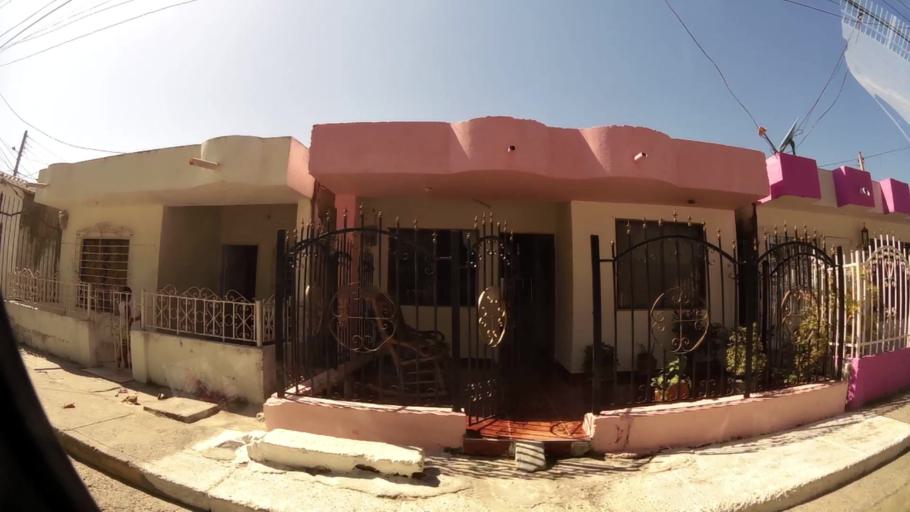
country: CO
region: Bolivar
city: Cartagena
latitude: 10.4381
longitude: -75.5145
